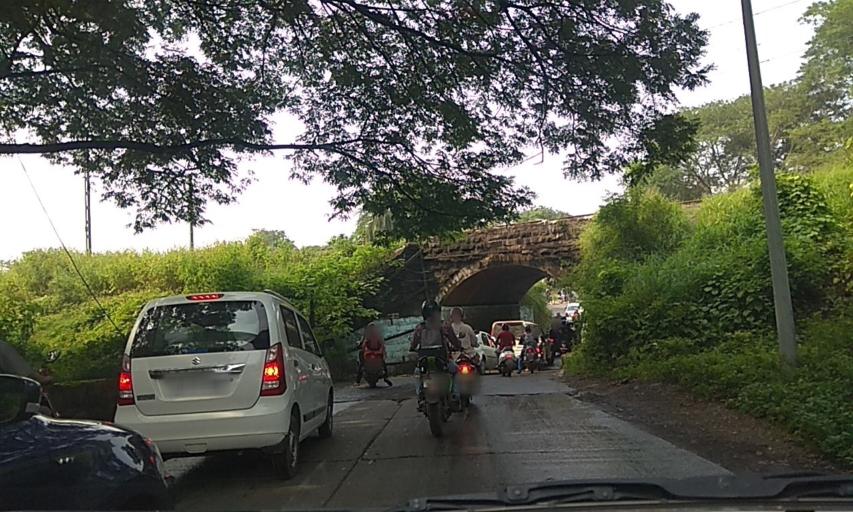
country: IN
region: Maharashtra
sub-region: Pune Division
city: Khadki
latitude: 18.5487
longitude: 73.8496
